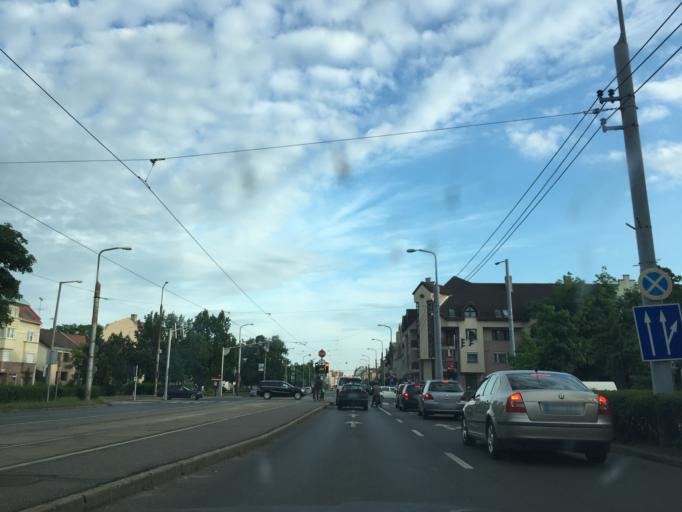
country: HU
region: Hajdu-Bihar
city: Debrecen
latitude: 47.5422
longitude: 21.6249
